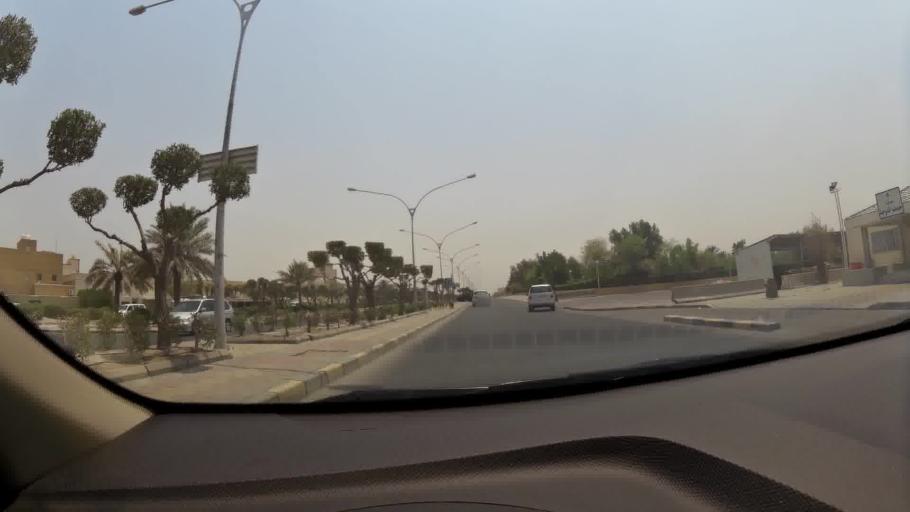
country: KW
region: Al Asimah
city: Ar Rabiyah
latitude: 29.3179
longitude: 47.8190
